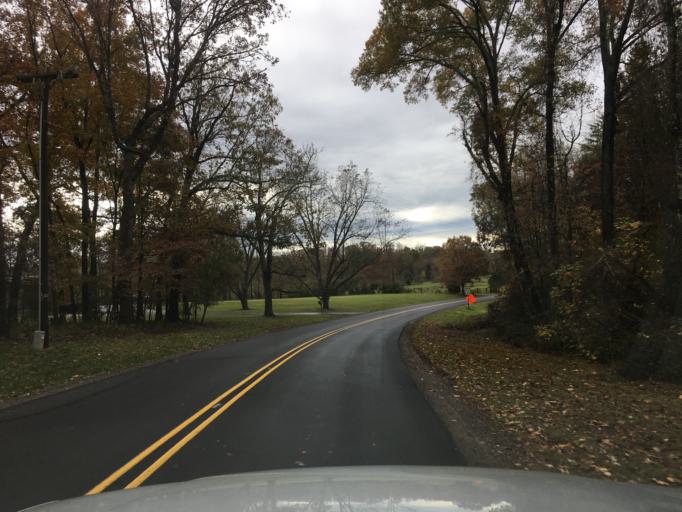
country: US
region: North Carolina
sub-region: Catawba County
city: Maiden
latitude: 35.6110
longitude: -81.2270
